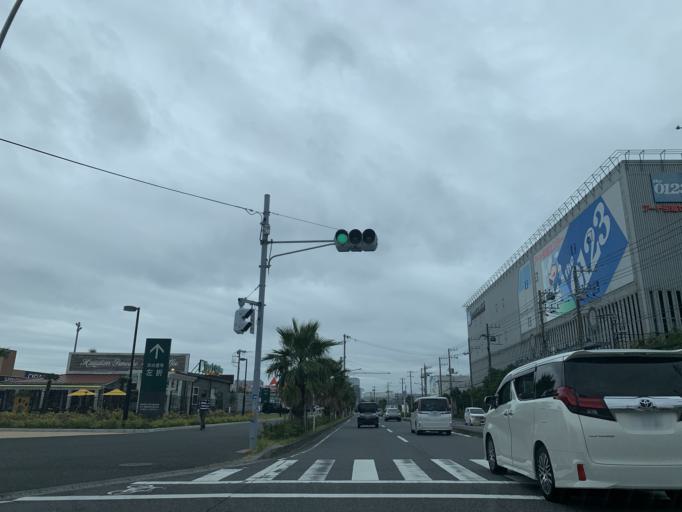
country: JP
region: Chiba
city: Funabashi
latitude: 35.6632
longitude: 140.0155
